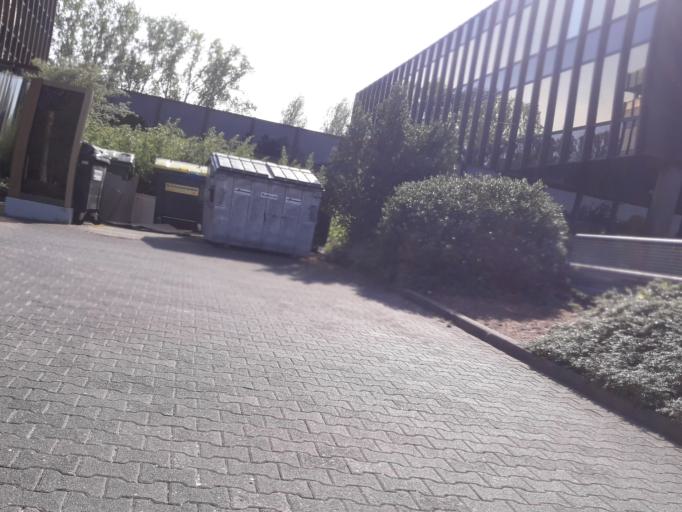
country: DE
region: North Rhine-Westphalia
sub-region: Regierungsbezirk Detmold
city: Paderborn
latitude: 51.7320
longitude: 8.7357
